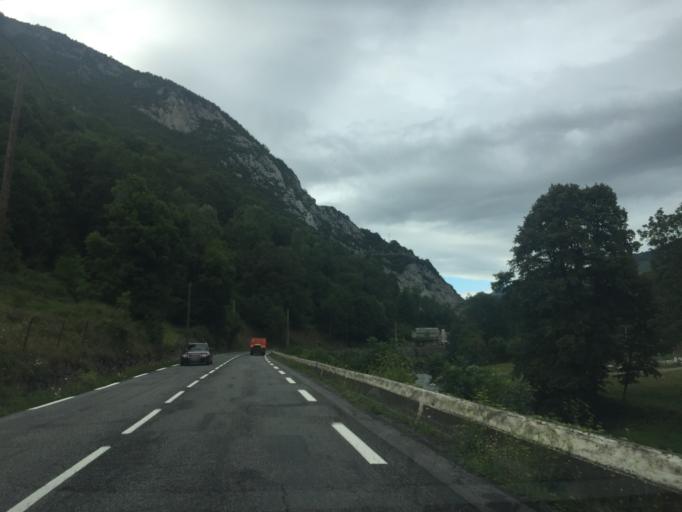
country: FR
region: Midi-Pyrenees
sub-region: Departement des Hautes-Pyrenees
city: La Barthe-de-Neste
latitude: 42.9453
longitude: 0.3737
